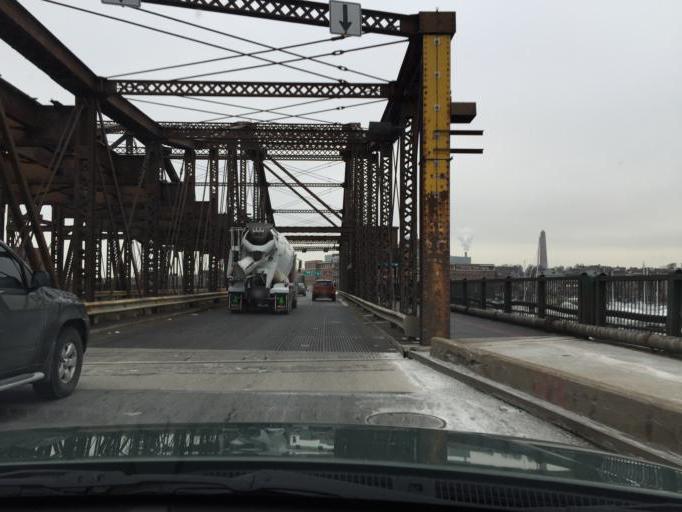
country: US
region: Massachusetts
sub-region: Suffolk County
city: Boston
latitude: 42.3683
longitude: -71.0594
